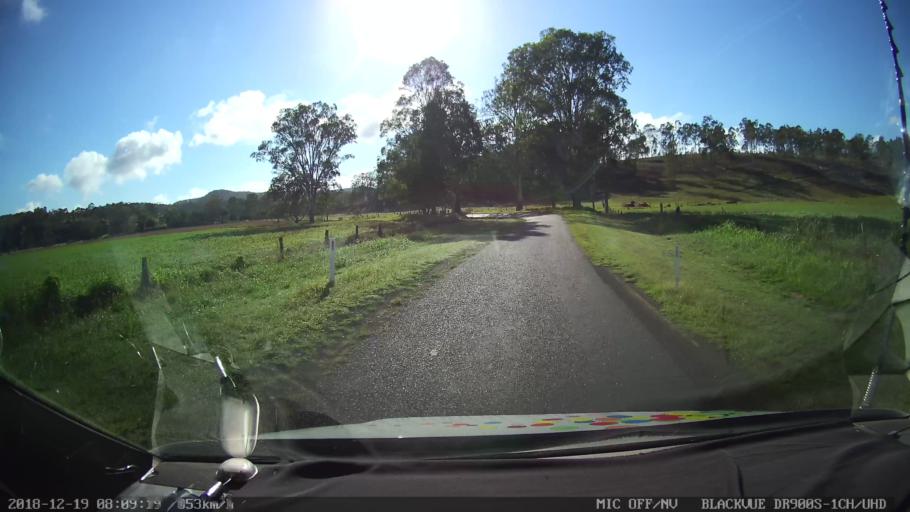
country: AU
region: Queensland
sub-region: Logan
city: Cedar Vale
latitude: -28.2140
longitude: 152.8777
